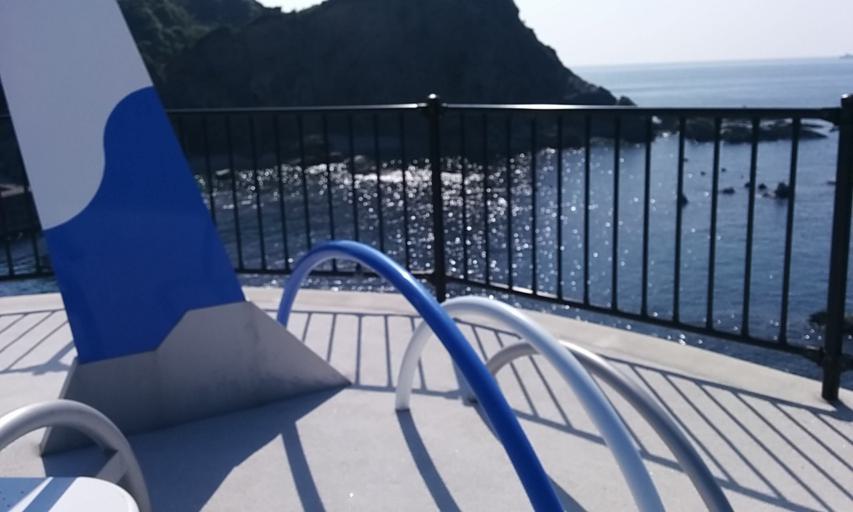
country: JP
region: Oita
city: Usuki
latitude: 33.3435
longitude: 132.0131
